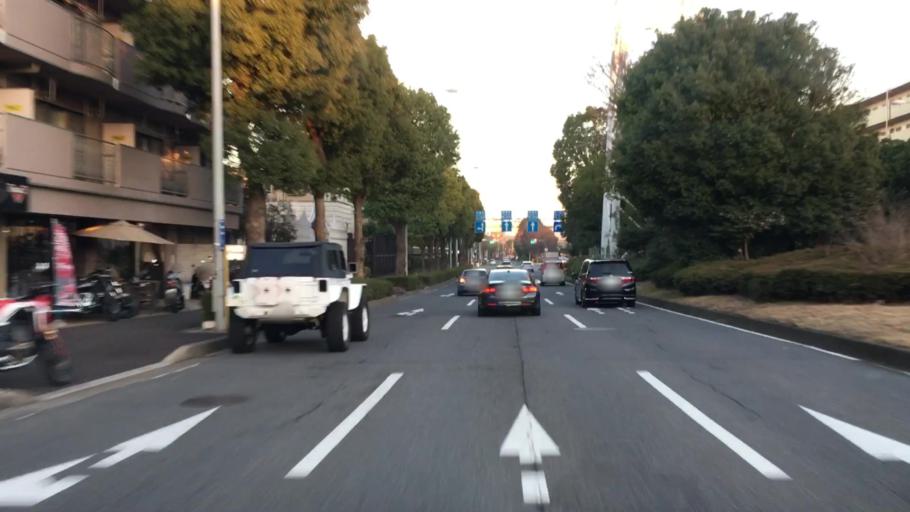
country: JP
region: Kanagawa
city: Yokohama
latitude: 35.5365
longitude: 139.5728
